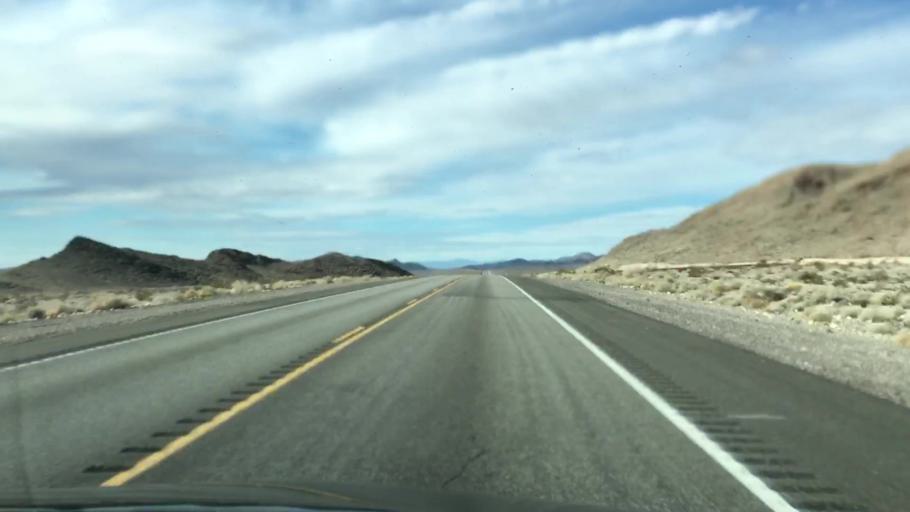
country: US
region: Nevada
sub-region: Nye County
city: Pahrump
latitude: 36.5804
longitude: -116.2013
